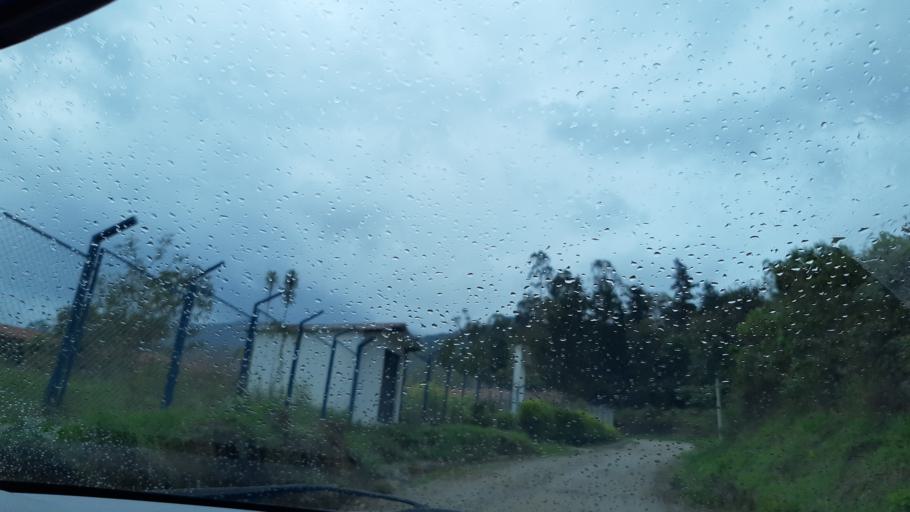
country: CO
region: Boyaca
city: Chivor
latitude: 4.9626
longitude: -73.3161
